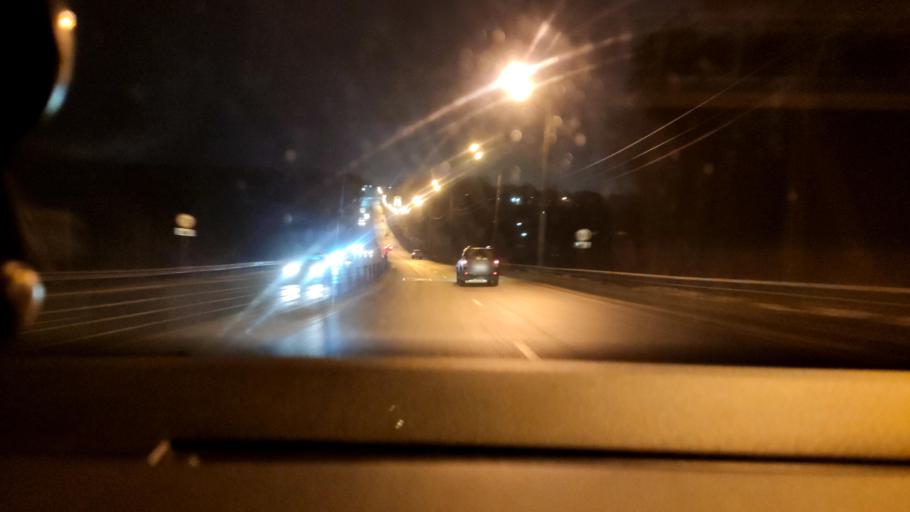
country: RU
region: Moskovskaya
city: Sergiyev Posad
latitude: 56.2630
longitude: 38.1272
